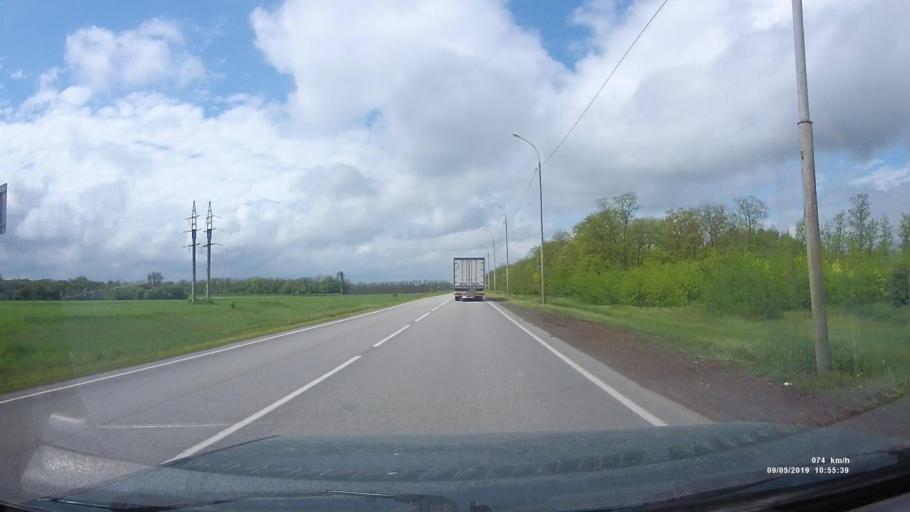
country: RU
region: Rostov
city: Peshkovo
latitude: 46.8720
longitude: 39.3118
